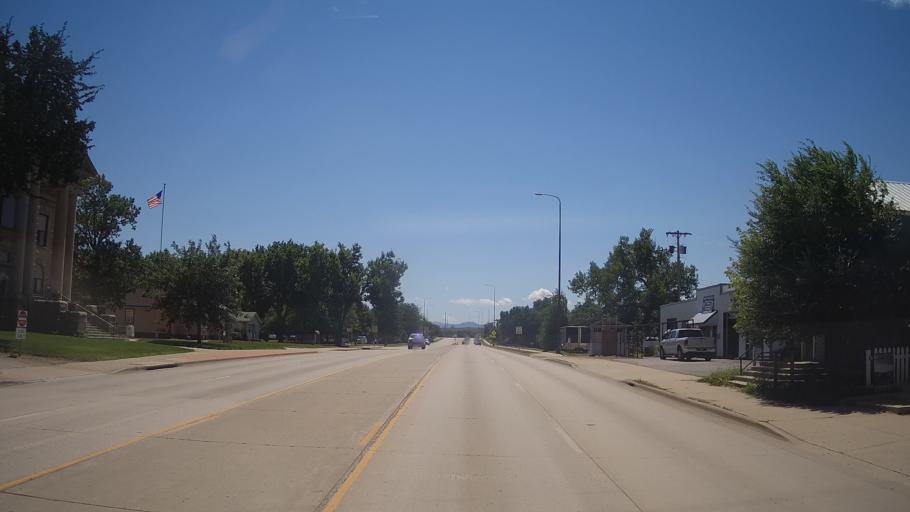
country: US
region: South Dakota
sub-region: Butte County
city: Belle Fourche
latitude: 44.6690
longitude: -103.8536
